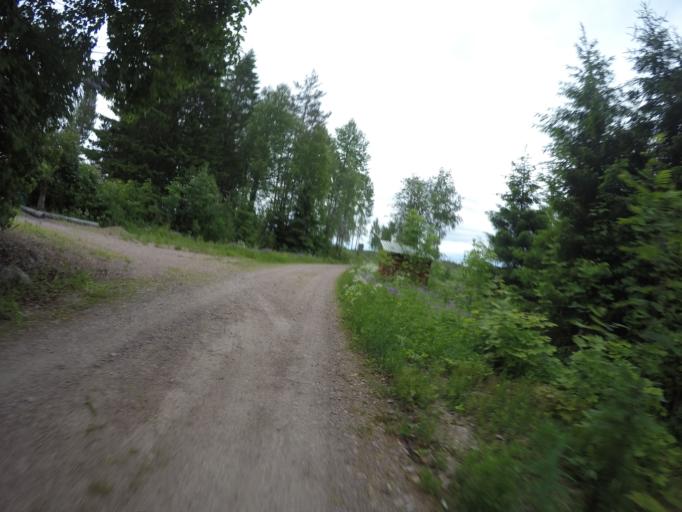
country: SE
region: Dalarna
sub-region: Ludvika Kommun
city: Abborrberget
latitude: 60.0800
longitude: 14.5568
